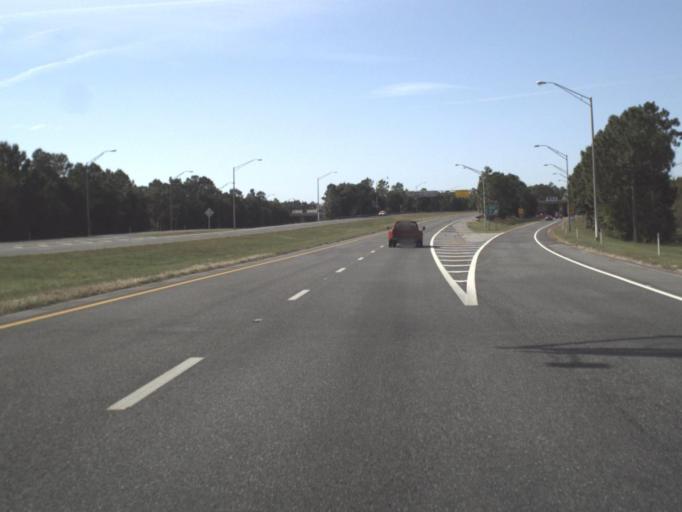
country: US
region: Florida
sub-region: Osceola County
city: Celebration
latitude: 28.3309
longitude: -81.5254
